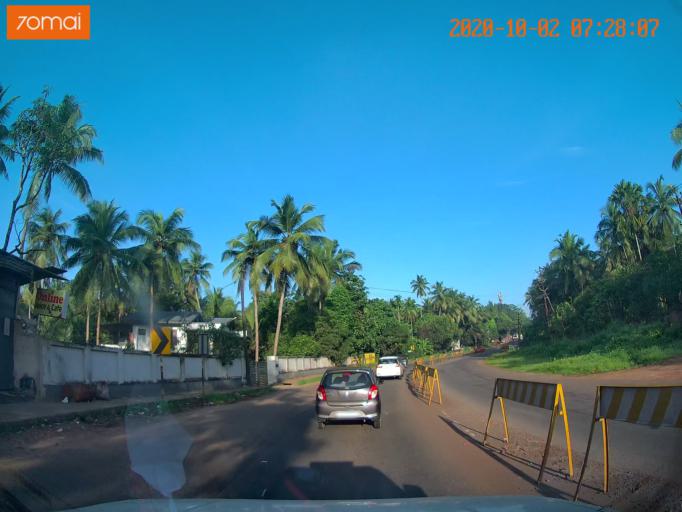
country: IN
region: Kerala
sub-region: Malappuram
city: Pariyapuram
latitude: 11.0274
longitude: 75.9446
